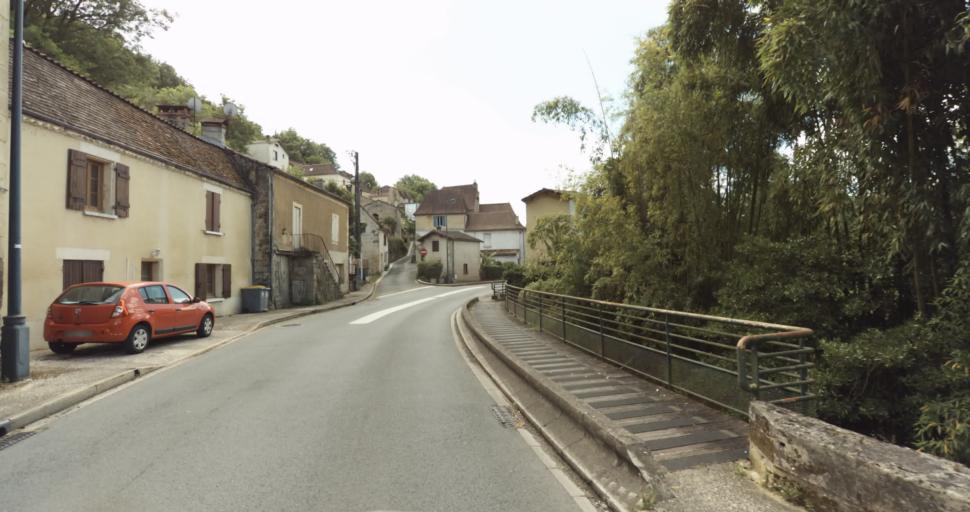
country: FR
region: Aquitaine
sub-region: Departement de la Dordogne
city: Lalinde
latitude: 44.8256
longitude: 0.7070
